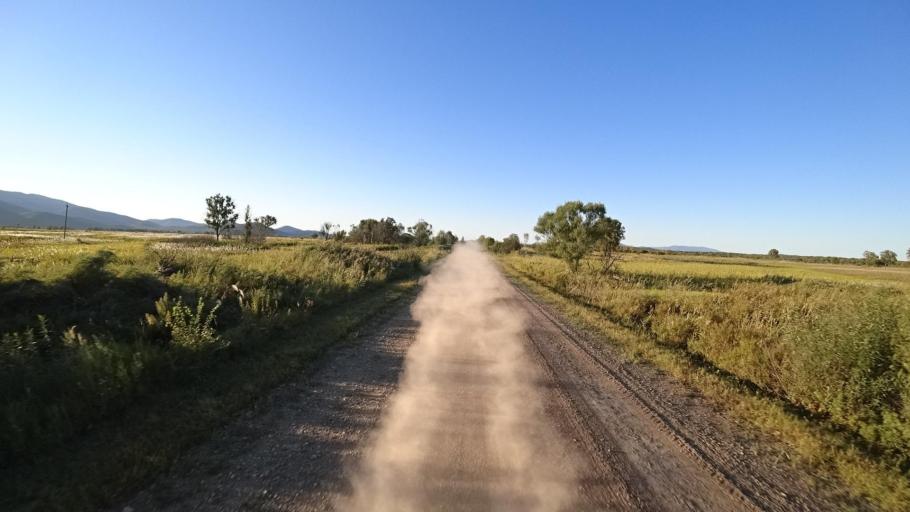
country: RU
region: Primorskiy
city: Kirovskiy
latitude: 44.7954
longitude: 133.6220
